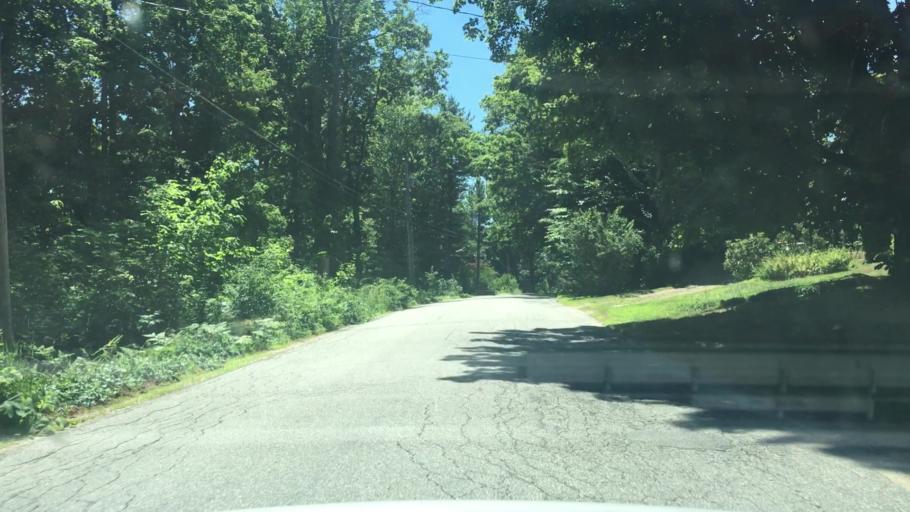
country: US
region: New Hampshire
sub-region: Merrimack County
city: Hopkinton
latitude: 43.2248
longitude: -71.6792
